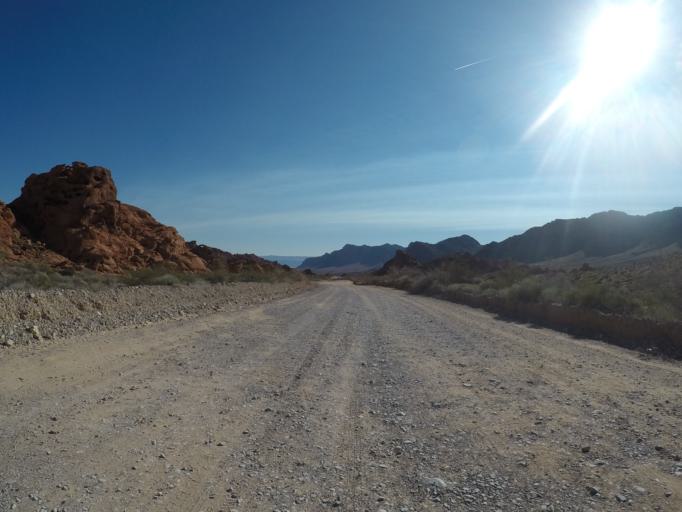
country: US
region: Nevada
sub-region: Clark County
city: Moapa Valley
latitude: 36.4125
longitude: -114.5565
